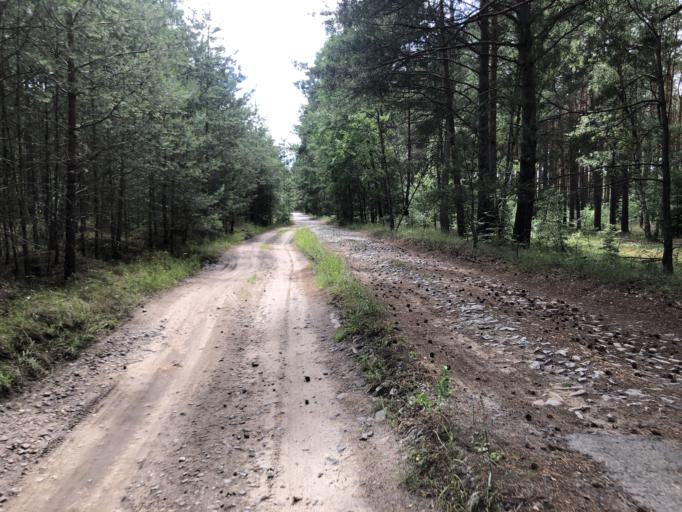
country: DE
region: Brandenburg
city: Biesenthal
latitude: 52.7923
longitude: 13.6628
